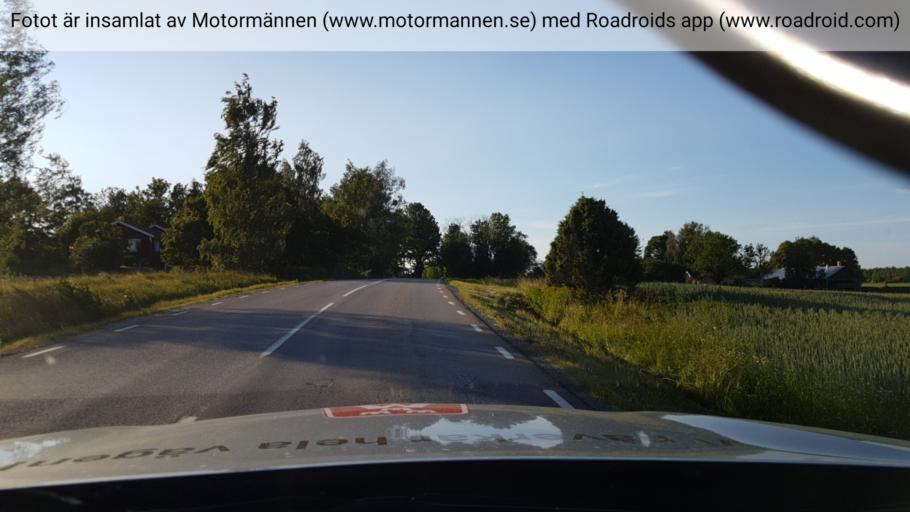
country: SE
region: Vaestmanland
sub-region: Surahammars Kommun
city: Ramnas
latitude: 59.9096
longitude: 16.3249
